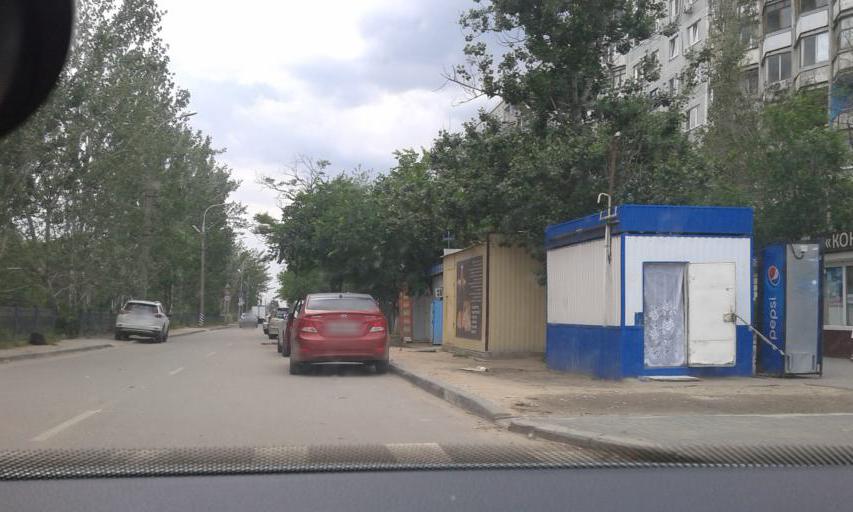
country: RU
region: Volgograd
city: Volgograd
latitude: 48.7544
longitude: 44.5037
